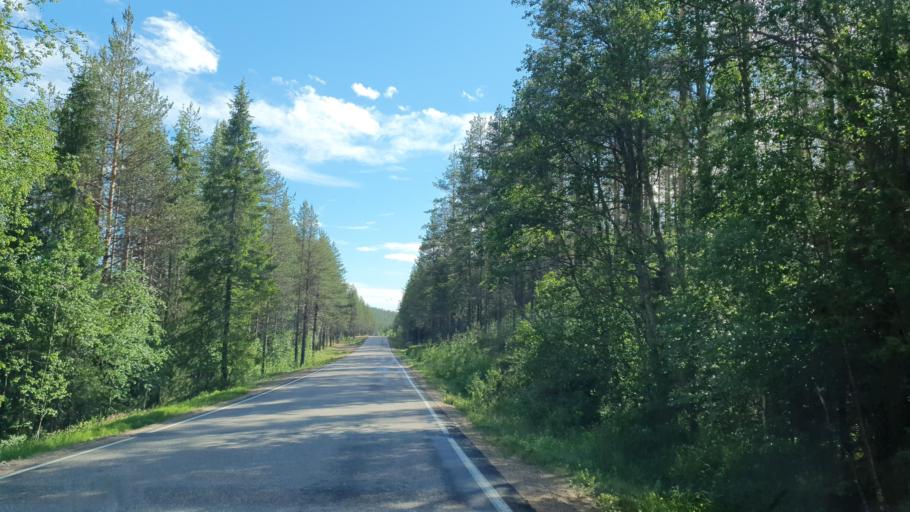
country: FI
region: Lapland
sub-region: Tunturi-Lappi
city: Kolari
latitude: 67.5737
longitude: 24.0563
